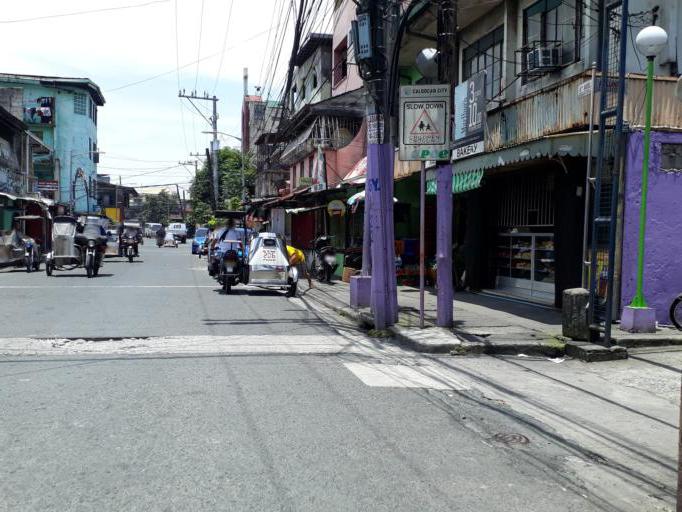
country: PH
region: Calabarzon
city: Del Monte
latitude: 14.6453
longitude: 120.9925
